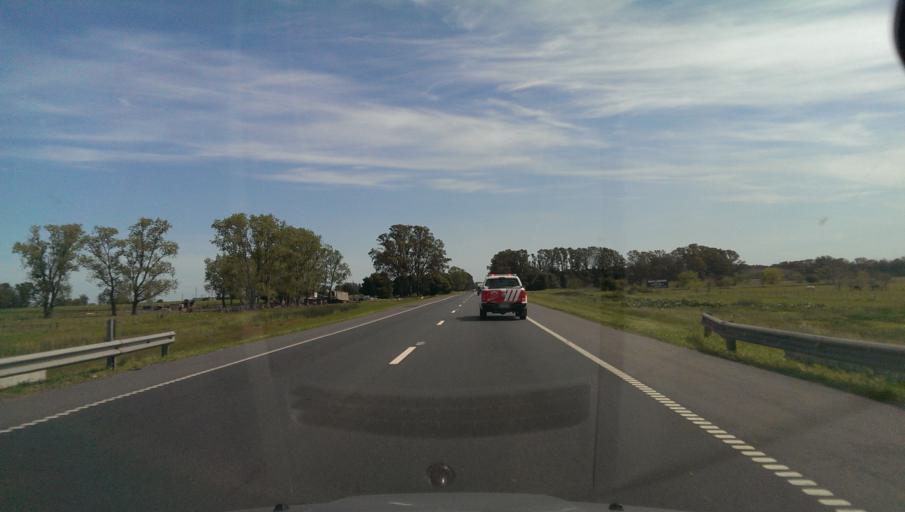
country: AR
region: Buenos Aires
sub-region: Partido de Las Flores
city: Las Flores
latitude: -36.3755
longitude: -59.4761
